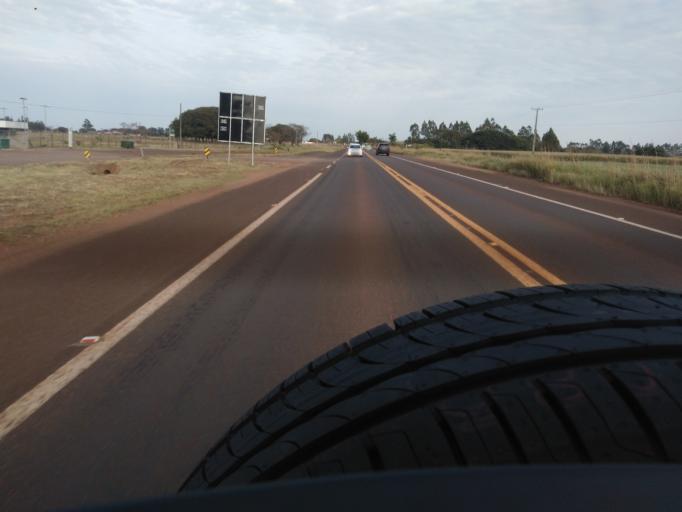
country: BR
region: Mato Grosso do Sul
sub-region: Ponta Pora
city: Ponta Pora
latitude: -22.6186
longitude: -55.6091
